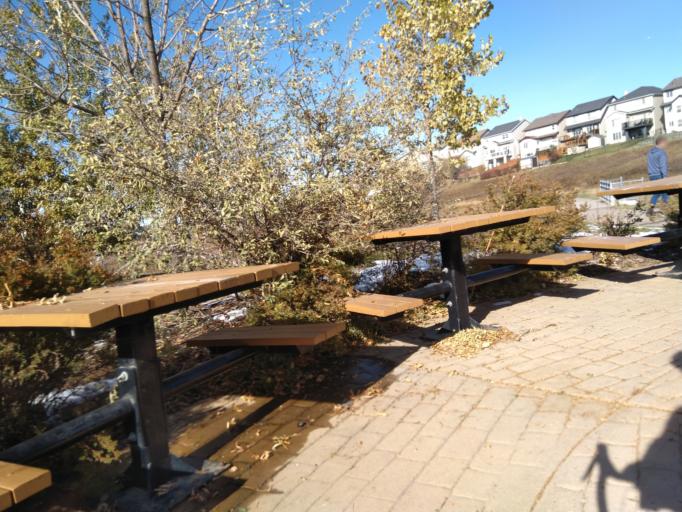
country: CA
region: Alberta
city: Calgary
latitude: 51.1623
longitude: -114.1237
